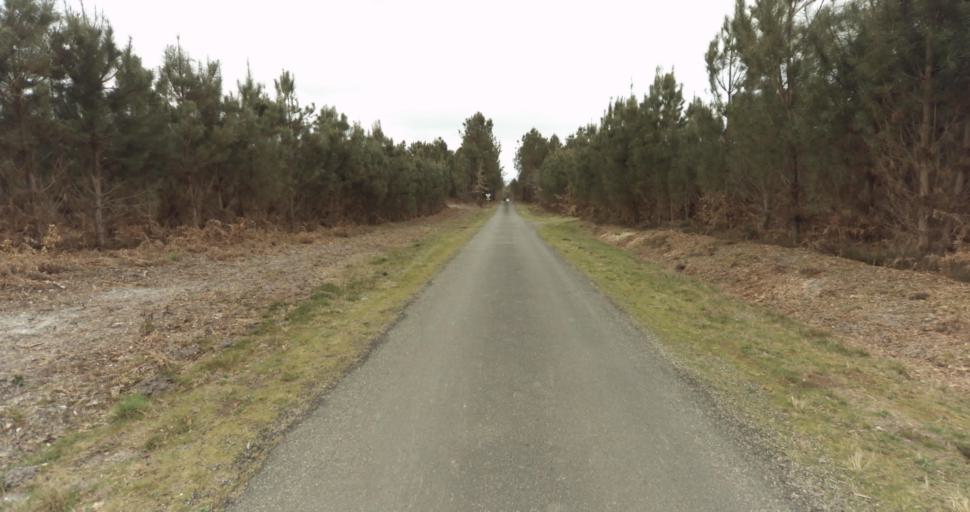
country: FR
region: Aquitaine
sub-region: Departement des Landes
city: Roquefort
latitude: 44.0585
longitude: -0.3914
